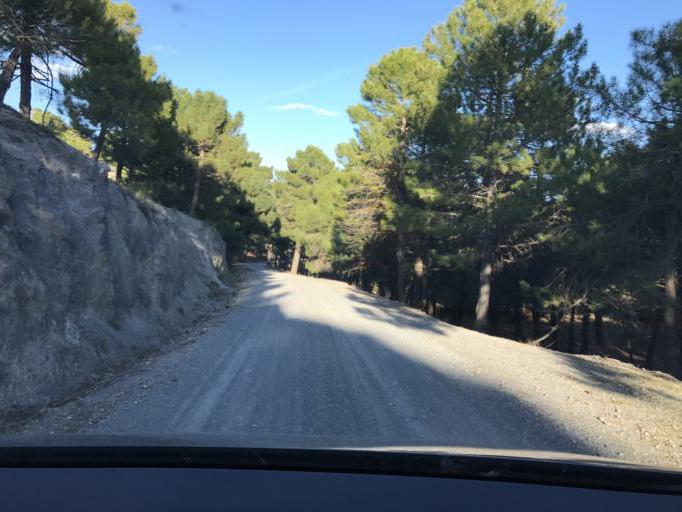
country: ES
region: Andalusia
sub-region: Provincia de Granada
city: Beas de Granada
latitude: 37.2341
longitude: -3.4377
